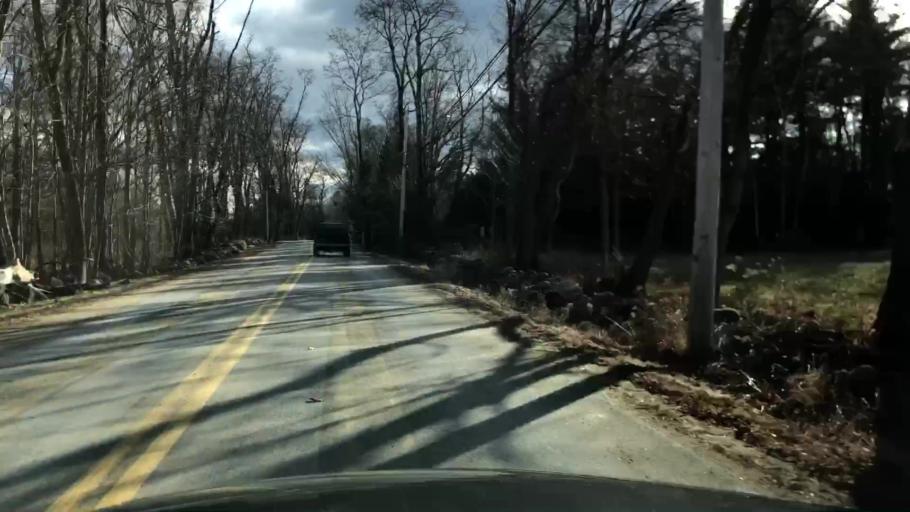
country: US
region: New Hampshire
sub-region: Hillsborough County
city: Mont Vernon
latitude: 42.8914
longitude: -71.6331
